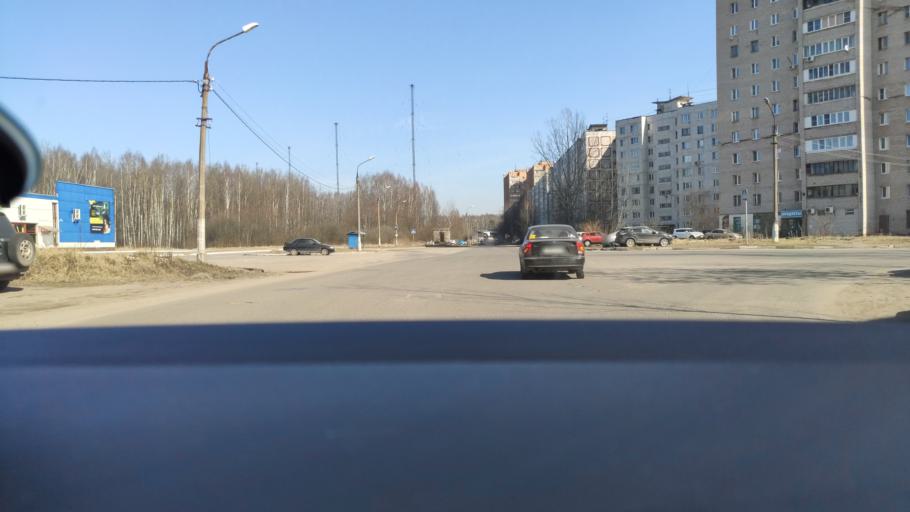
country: RU
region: Moskovskaya
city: Elektrostal'
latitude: 55.7694
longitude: 38.4167
